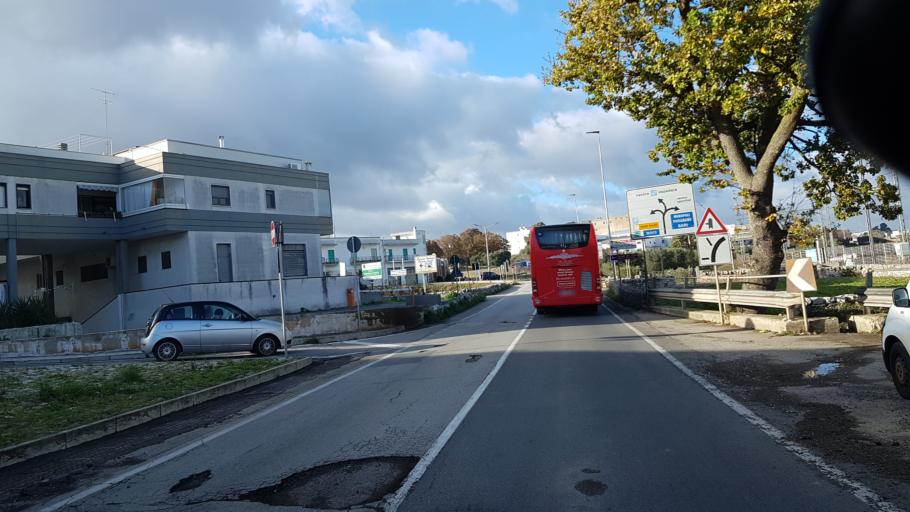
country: IT
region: Apulia
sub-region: Provincia di Bari
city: Alberobello
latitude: 40.7813
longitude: 17.2451
